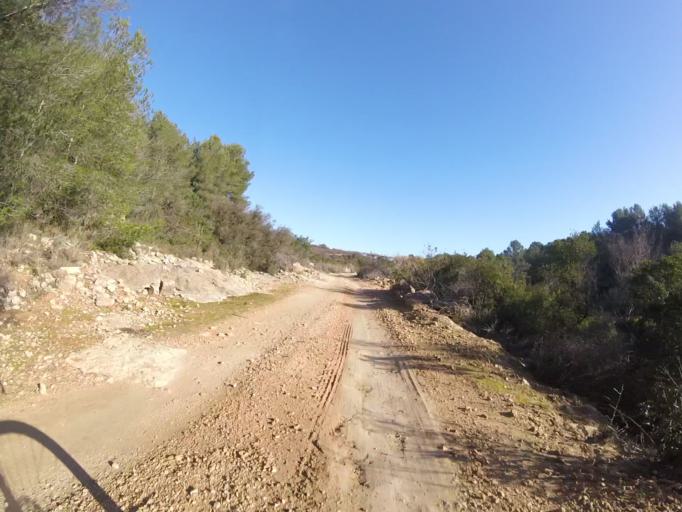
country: ES
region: Valencia
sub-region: Provincia de Castello
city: Torreblanca
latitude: 40.2540
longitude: 0.1896
